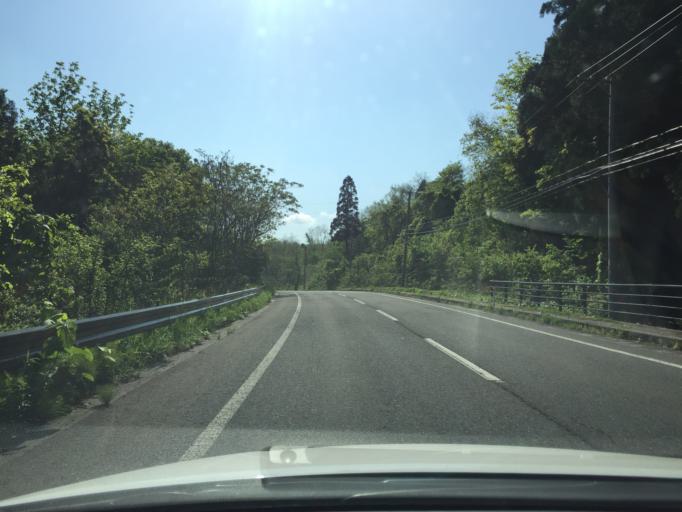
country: JP
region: Niigata
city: Suibara
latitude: 37.7017
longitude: 139.4701
